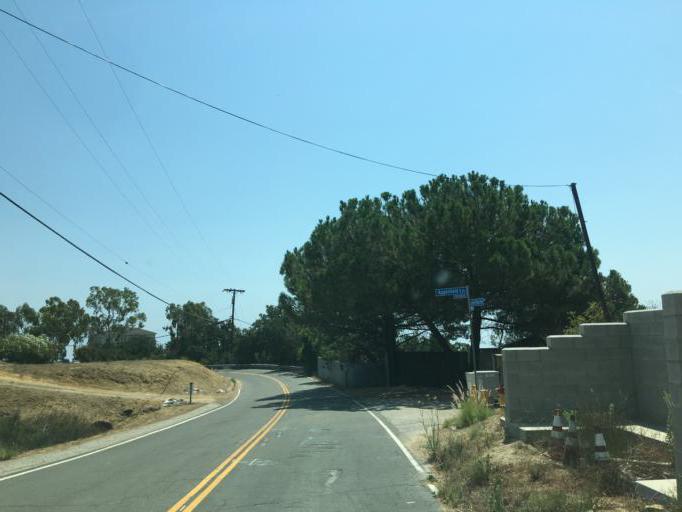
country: US
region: California
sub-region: Los Angeles County
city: Topanga
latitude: 34.0692
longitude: -118.6159
